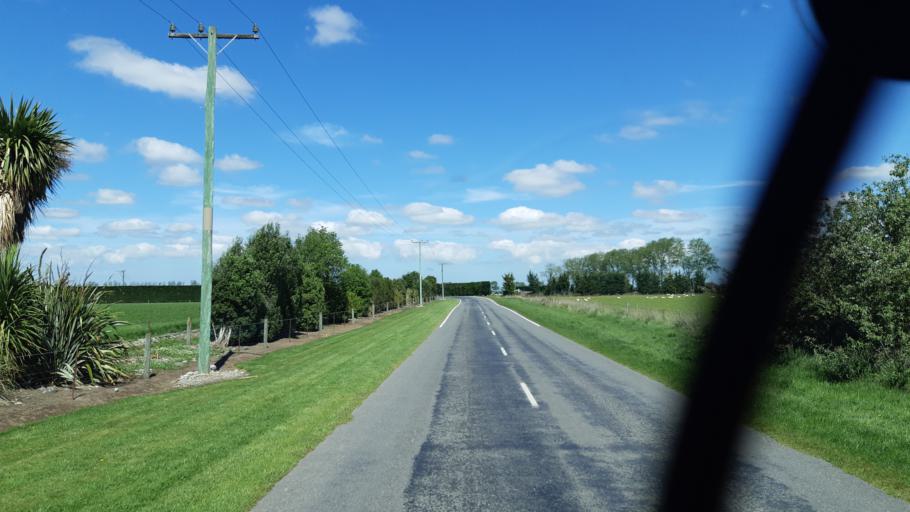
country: NZ
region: Canterbury
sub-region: Ashburton District
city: Tinwald
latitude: -43.8632
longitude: 171.4478
